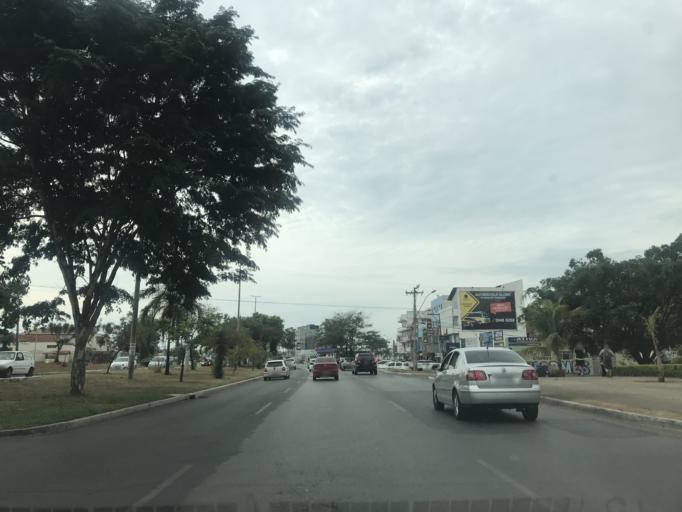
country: BR
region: Federal District
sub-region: Brasilia
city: Brasilia
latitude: -15.8425
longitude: -47.9828
